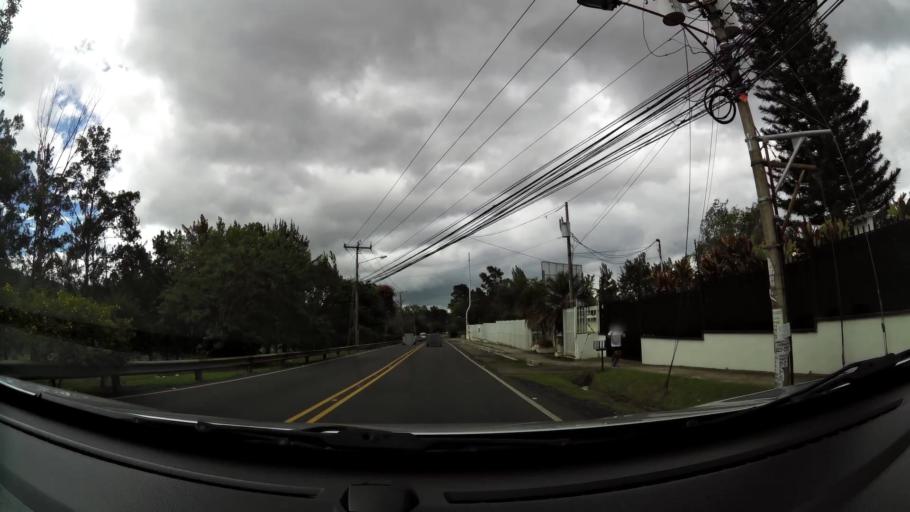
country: CR
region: San Jose
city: Curridabat
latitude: 9.9129
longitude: -84.0248
